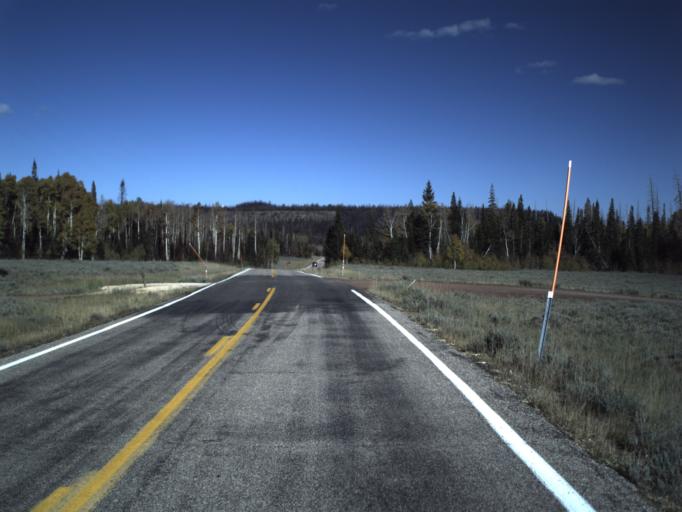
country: US
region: Utah
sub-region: Iron County
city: Parowan
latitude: 37.6590
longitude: -112.7434
